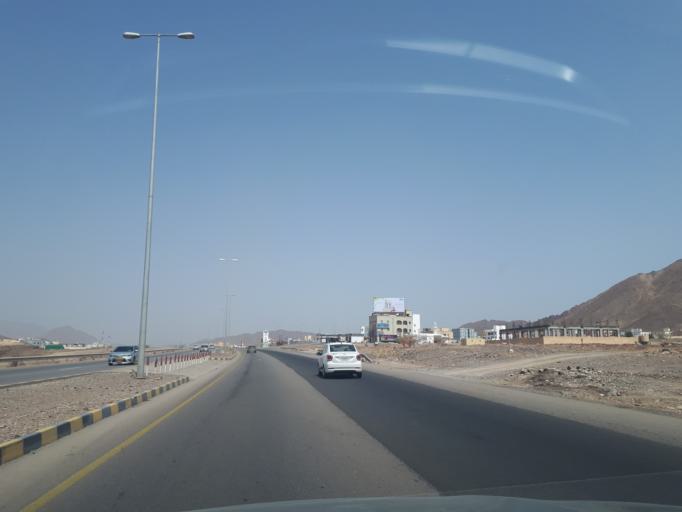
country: OM
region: Muhafazat ad Dakhiliyah
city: Bidbid
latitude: 23.4609
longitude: 58.1651
